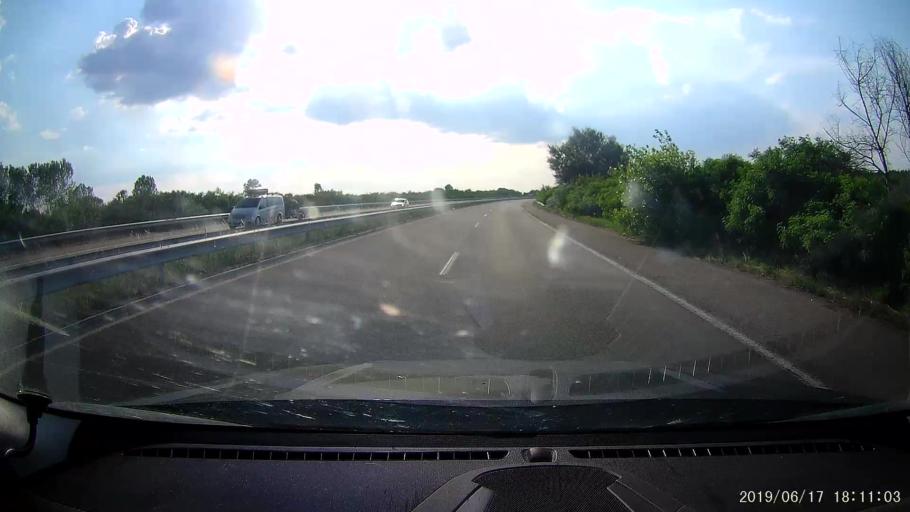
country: BG
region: Khaskovo
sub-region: Obshtina Lyubimets
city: Lyubimets
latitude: 41.8785
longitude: 26.0606
